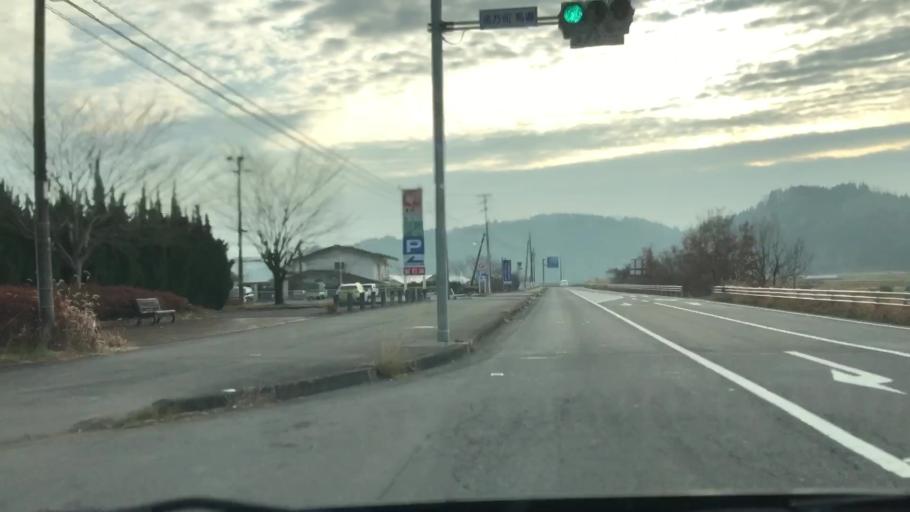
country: JP
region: Oita
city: Takedamachi
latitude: 32.9662
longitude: 131.4812
